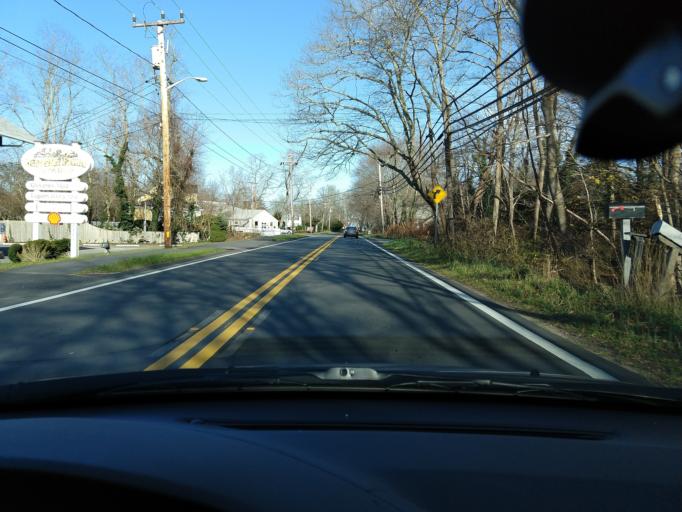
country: US
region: Massachusetts
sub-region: Barnstable County
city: Brewster
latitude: 41.7694
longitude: -70.0551
